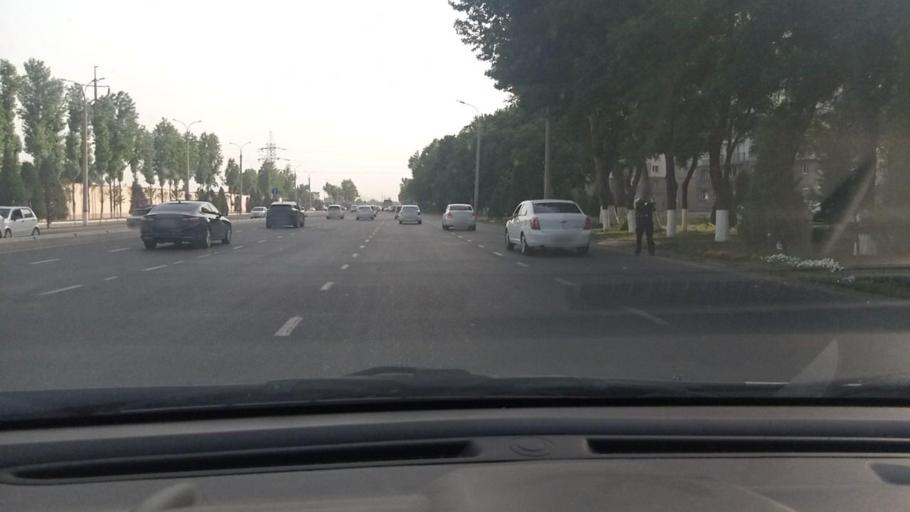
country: UZ
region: Toshkent
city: Salor
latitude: 41.3229
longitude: 69.3643
